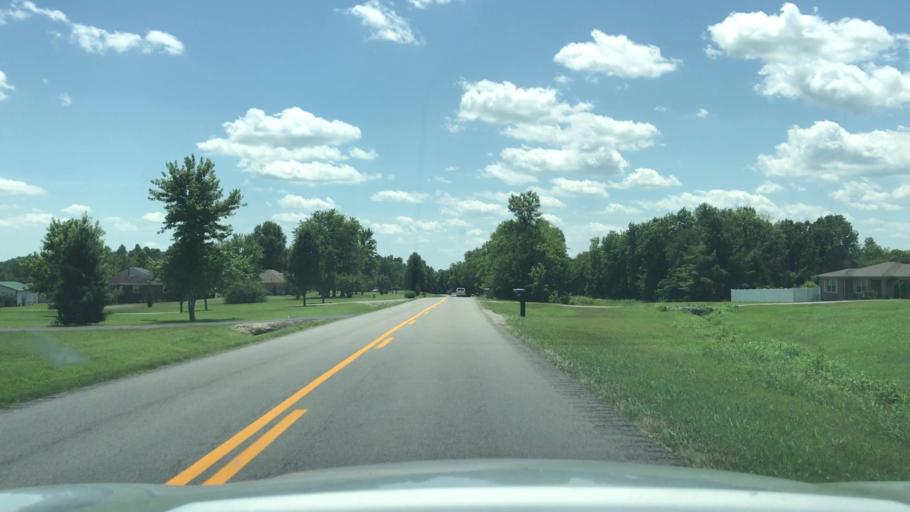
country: US
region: Kentucky
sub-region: Christian County
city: Hopkinsville
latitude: 36.9156
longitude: -87.4402
